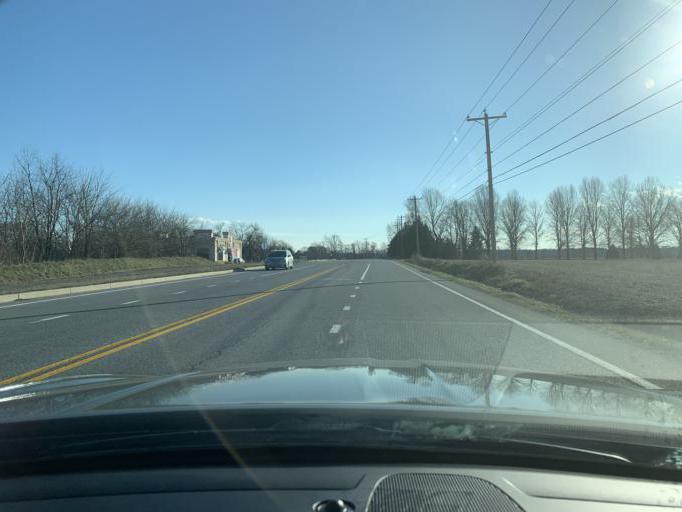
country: US
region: Maryland
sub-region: Queen Anne's County
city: Centreville
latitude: 39.0305
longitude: -76.0773
